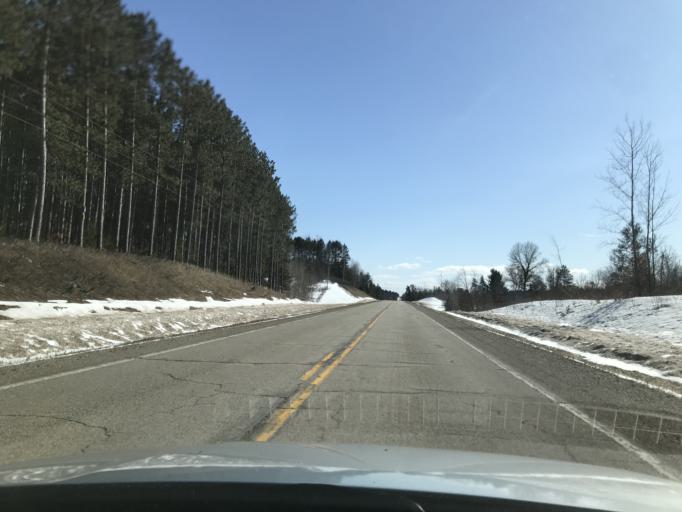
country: US
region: Wisconsin
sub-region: Marinette County
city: Niagara
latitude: 45.3798
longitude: -88.0999
